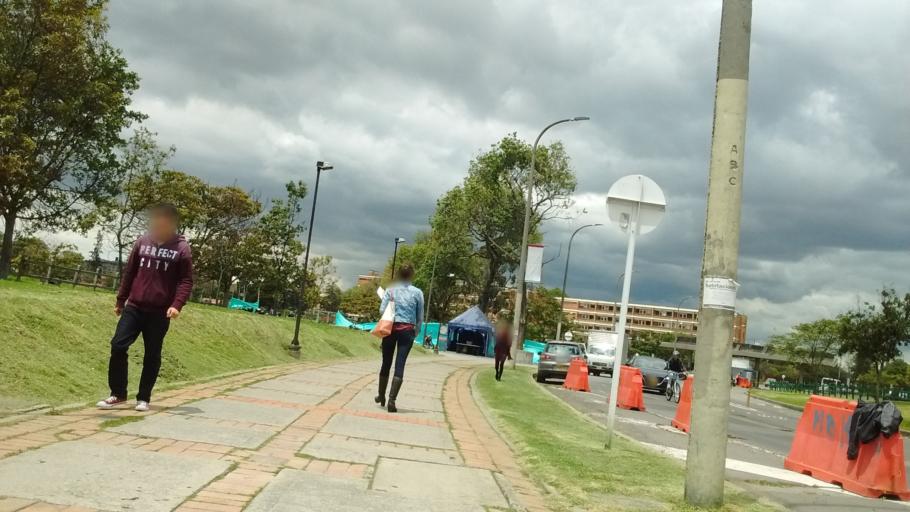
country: CO
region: Bogota D.C.
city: Bogota
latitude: 4.6386
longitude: -74.0881
